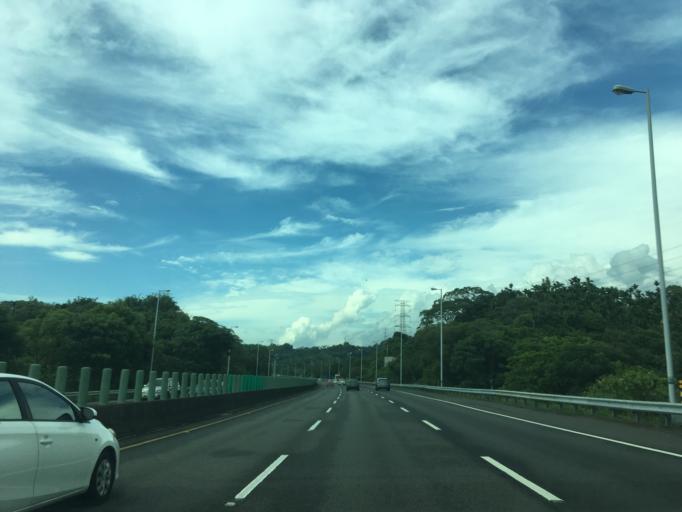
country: TW
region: Taiwan
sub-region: Chiayi
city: Jiayi Shi
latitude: 23.4638
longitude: 120.4968
